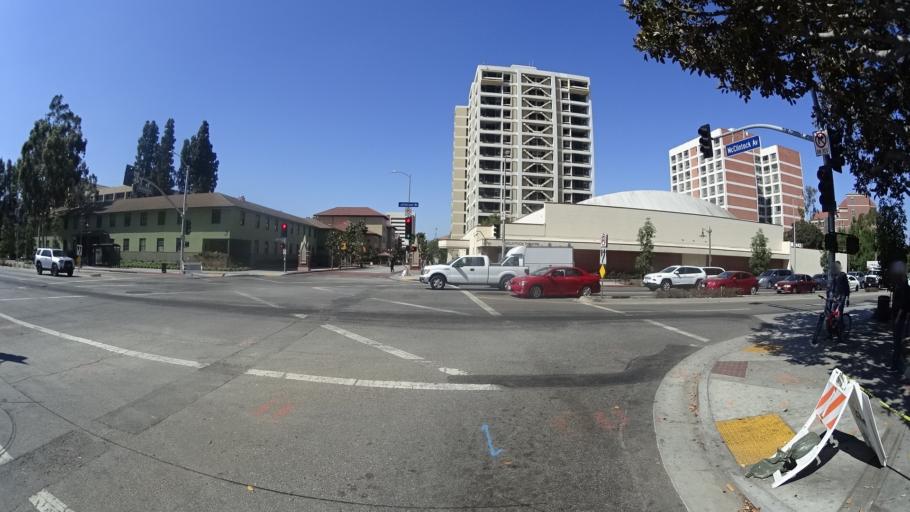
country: US
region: California
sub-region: Los Angeles County
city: Los Angeles
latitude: 34.0252
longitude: -118.2871
